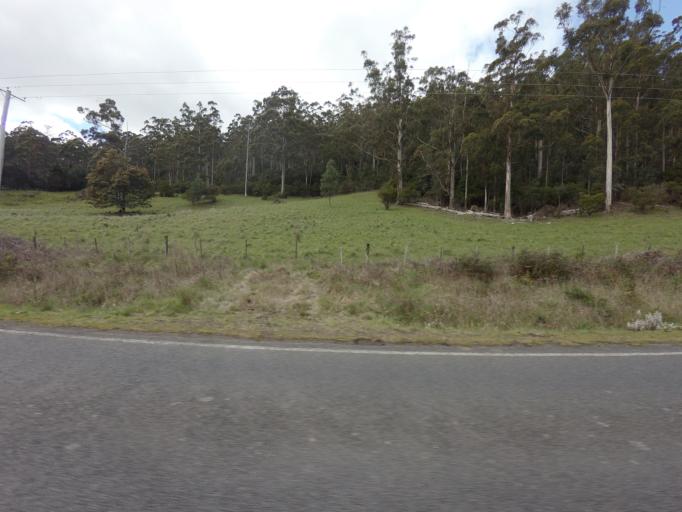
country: AU
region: Tasmania
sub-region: Huon Valley
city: Cygnet
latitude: -43.2791
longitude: 147.0094
